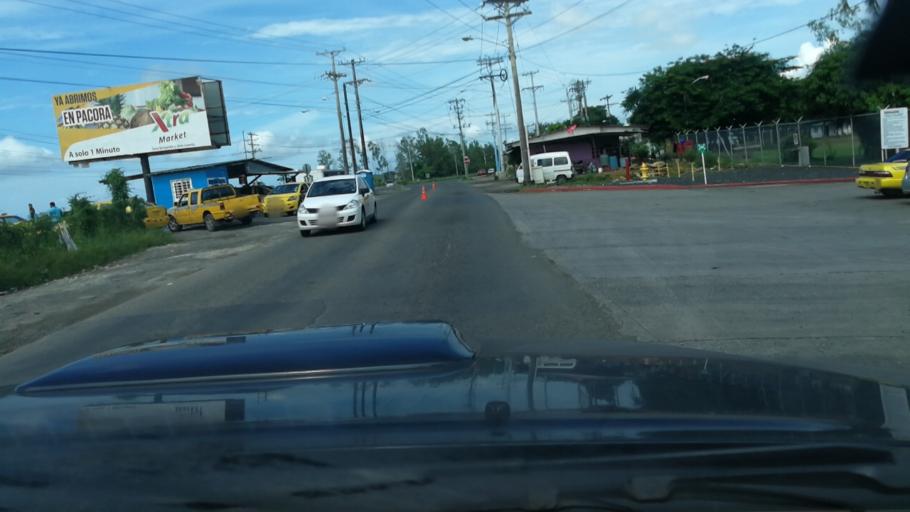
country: PA
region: Panama
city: Los Lotes
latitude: 9.1044
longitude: -79.2722
